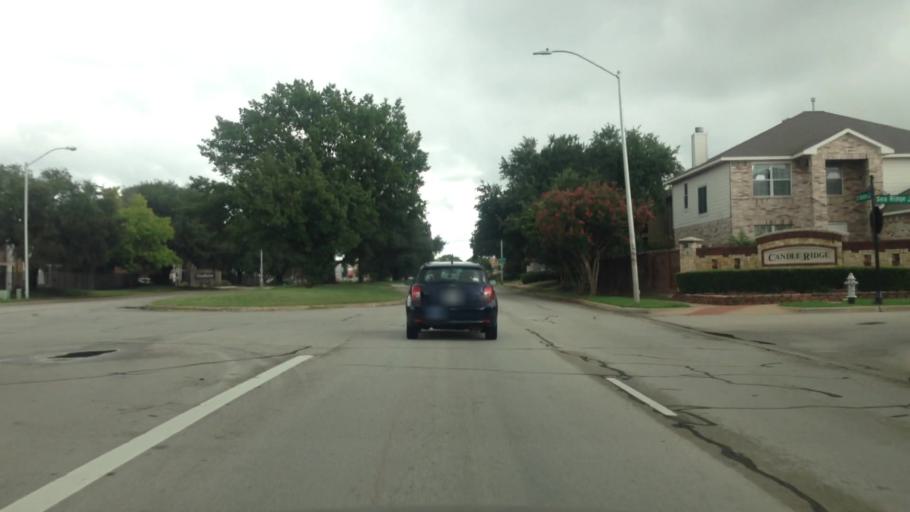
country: US
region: Texas
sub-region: Tarrant County
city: Edgecliff Village
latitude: 32.6361
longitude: -97.3931
